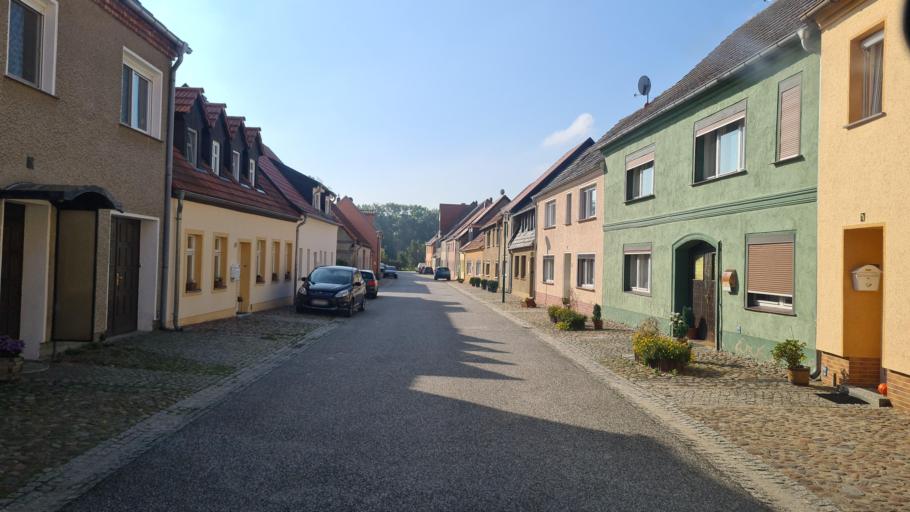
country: DE
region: Brandenburg
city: Luckau
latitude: 51.8509
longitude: 13.7196
